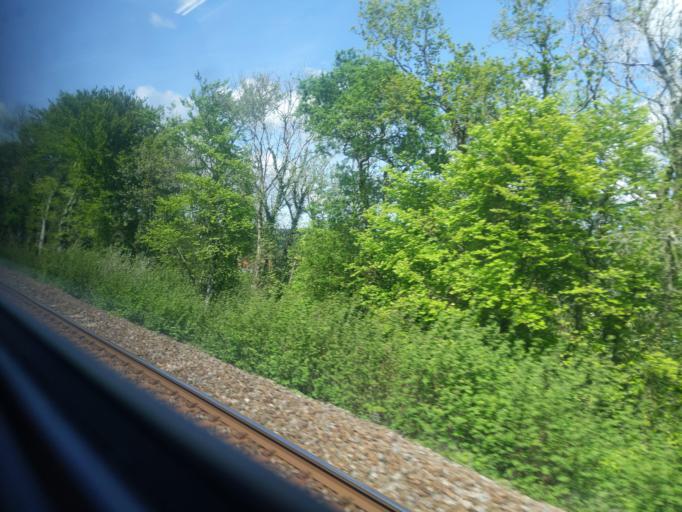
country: GB
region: England
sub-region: Cornwall
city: Liskeard
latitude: 50.4537
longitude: -4.4962
